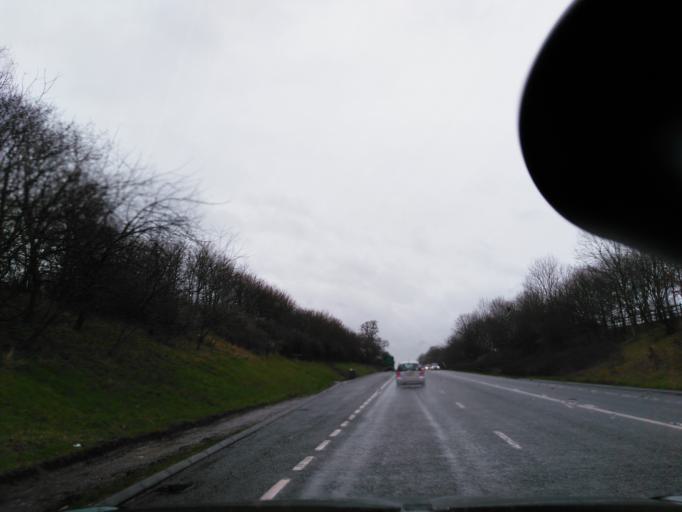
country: GB
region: England
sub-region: Wiltshire
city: Chapmanslade
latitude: 51.2579
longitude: -2.2824
